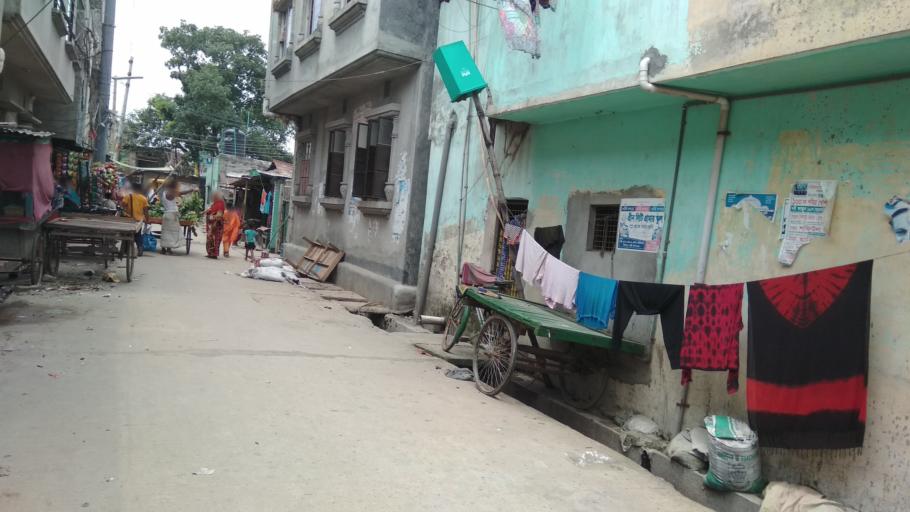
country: BD
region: Dhaka
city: Tungi
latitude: 23.8179
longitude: 90.3788
